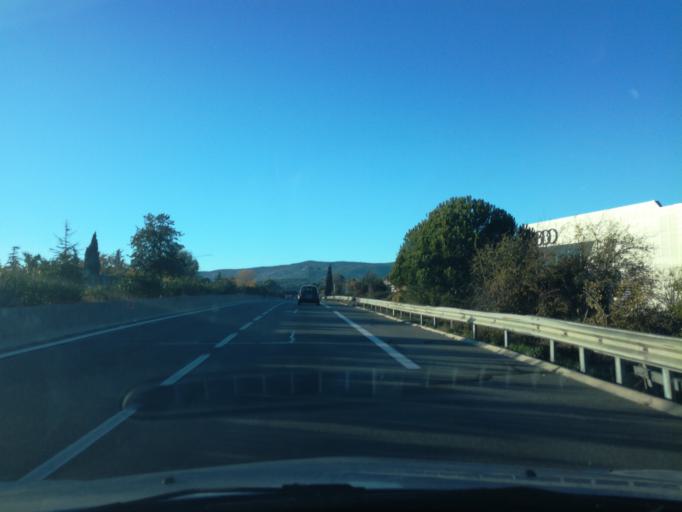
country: FR
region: Provence-Alpes-Cote d'Azur
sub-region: Departement des Alpes-Maritimes
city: Mouans-Sartoux
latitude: 43.6097
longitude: 6.9727
